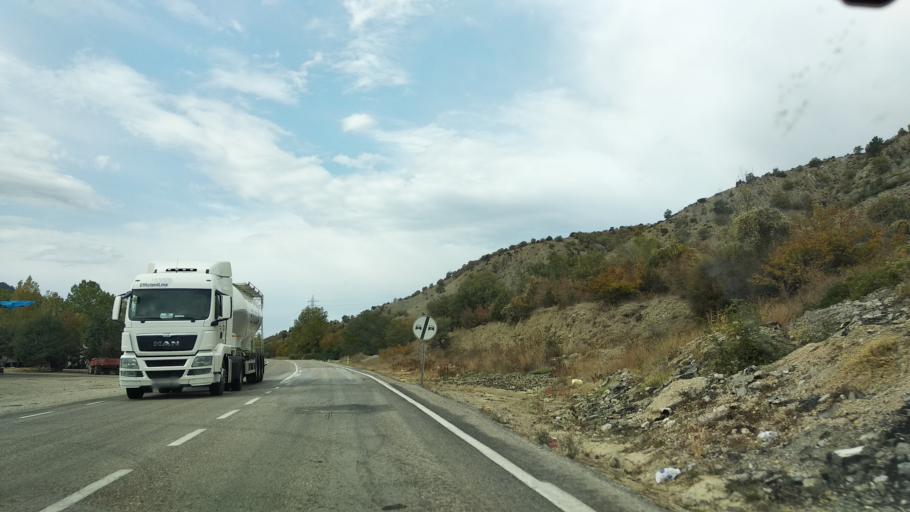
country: TR
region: Ankara
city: Nallihan
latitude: 40.3081
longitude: 31.2865
